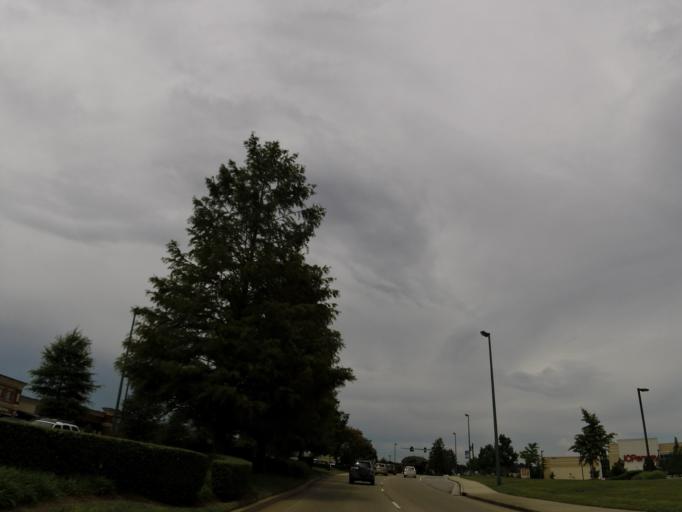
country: US
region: Tennessee
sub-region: Knox County
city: Farragut
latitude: 35.8958
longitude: -84.1706
